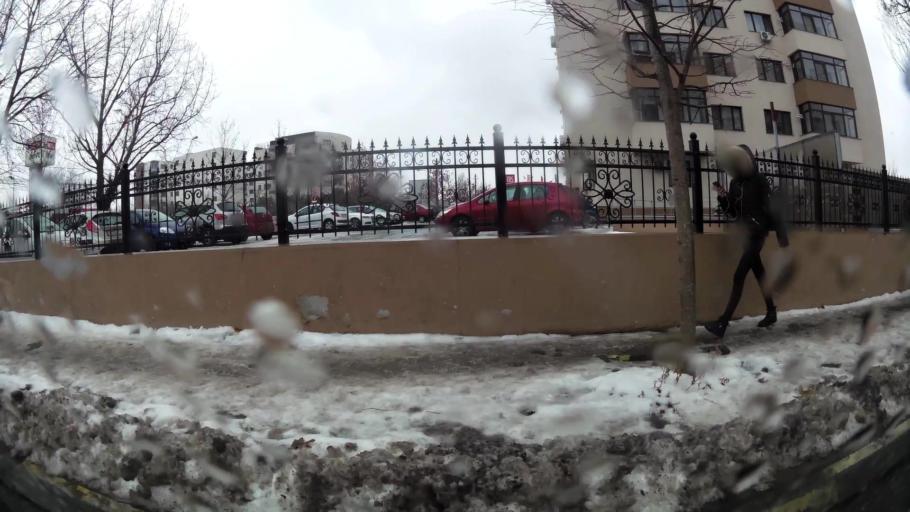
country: RO
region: Ilfov
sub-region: Comuna Chiajna
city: Rosu
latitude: 44.4120
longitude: 26.0152
